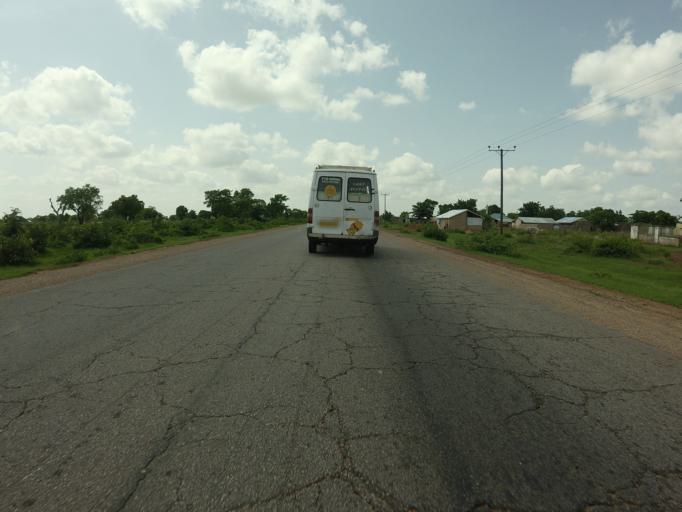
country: GH
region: Northern
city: Savelugu
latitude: 9.5873
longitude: -0.8328
